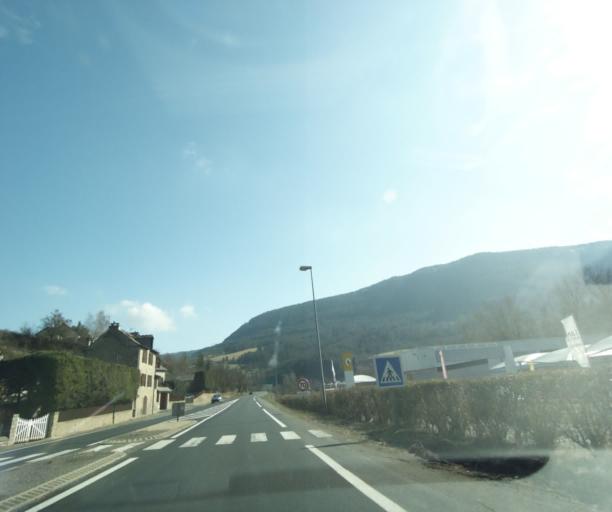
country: FR
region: Languedoc-Roussillon
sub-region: Departement de la Lozere
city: Mende
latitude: 44.5260
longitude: 3.5159
